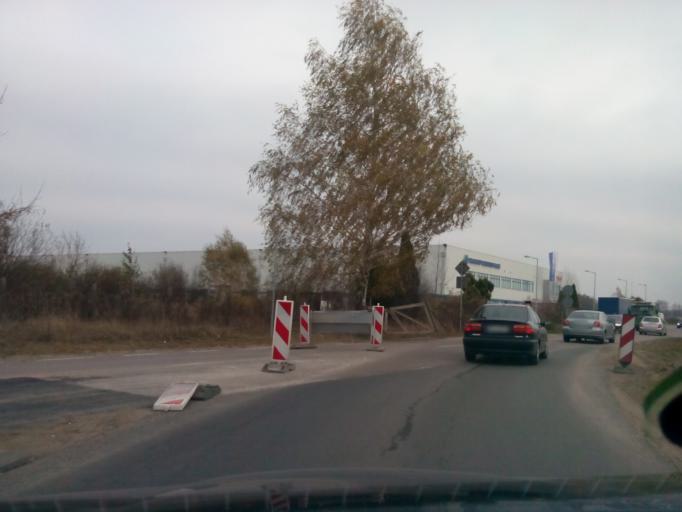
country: PL
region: Masovian Voivodeship
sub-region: Powiat pruszkowski
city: Nowe Grocholice
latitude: 52.1445
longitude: 20.8915
